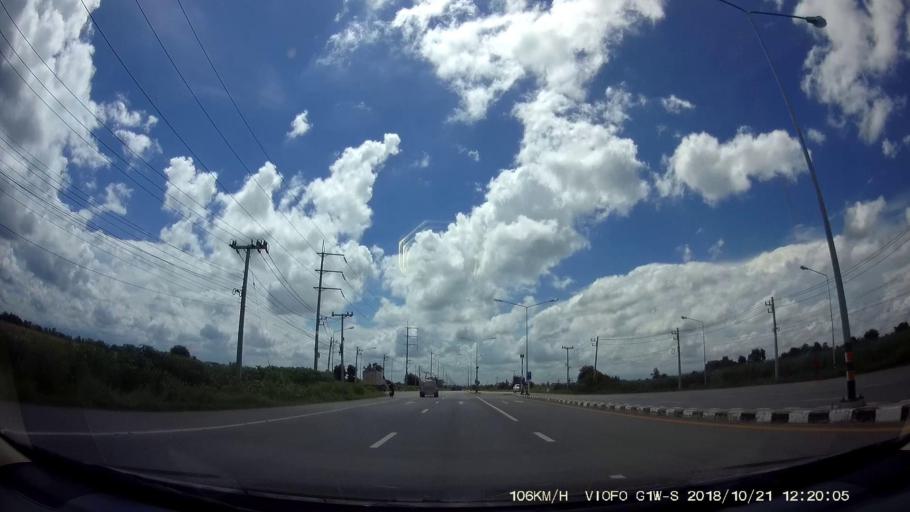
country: TH
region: Nakhon Ratchasima
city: Dan Khun Thot
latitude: 15.2924
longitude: 101.8067
